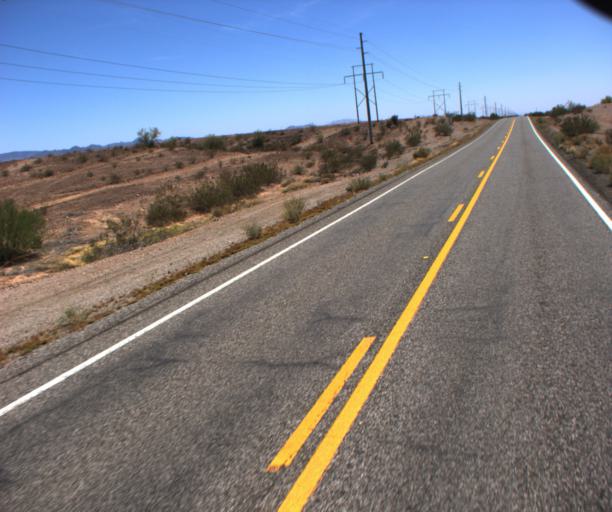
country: US
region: Arizona
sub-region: La Paz County
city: Quartzsite
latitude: 33.7621
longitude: -114.2170
